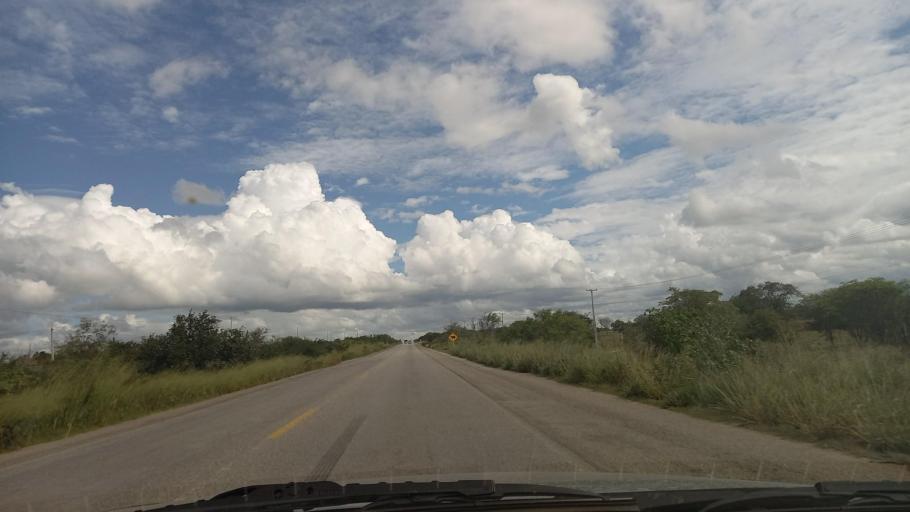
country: BR
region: Pernambuco
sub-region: Cachoeirinha
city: Cachoeirinha
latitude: -8.4377
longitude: -36.2039
